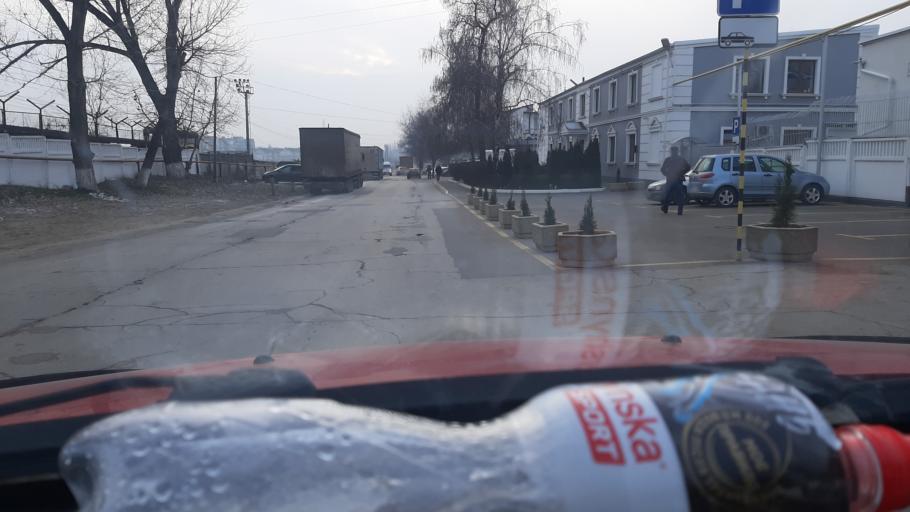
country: MD
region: Chisinau
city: Chisinau
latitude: 46.9867
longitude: 28.8852
